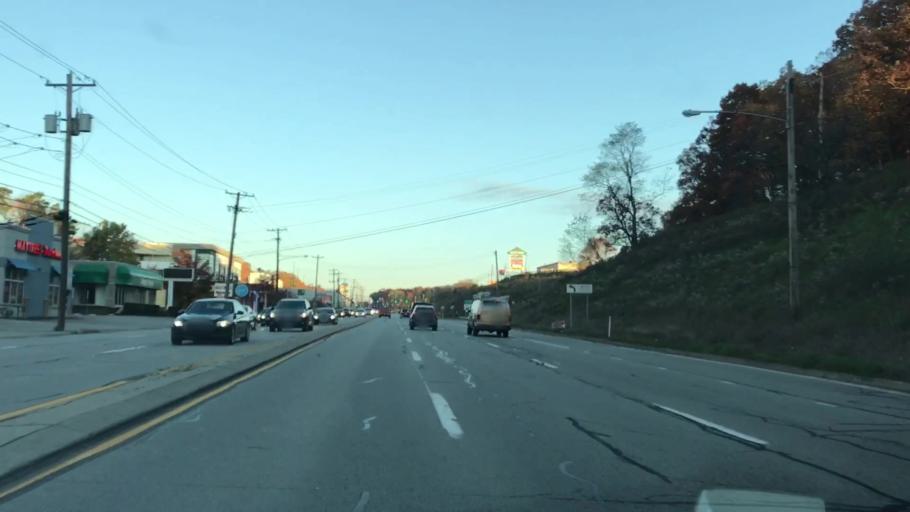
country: US
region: Pennsylvania
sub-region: Allegheny County
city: West View
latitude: 40.5478
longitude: -80.0181
